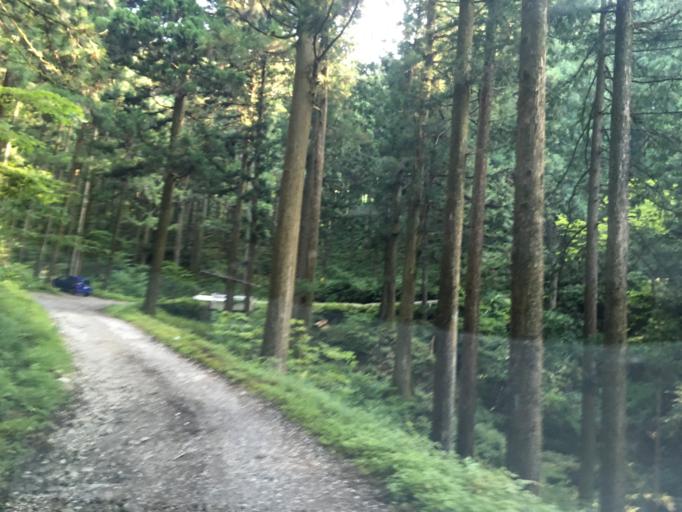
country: JP
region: Saitama
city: Chichibu
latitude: 35.9415
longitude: 139.1167
